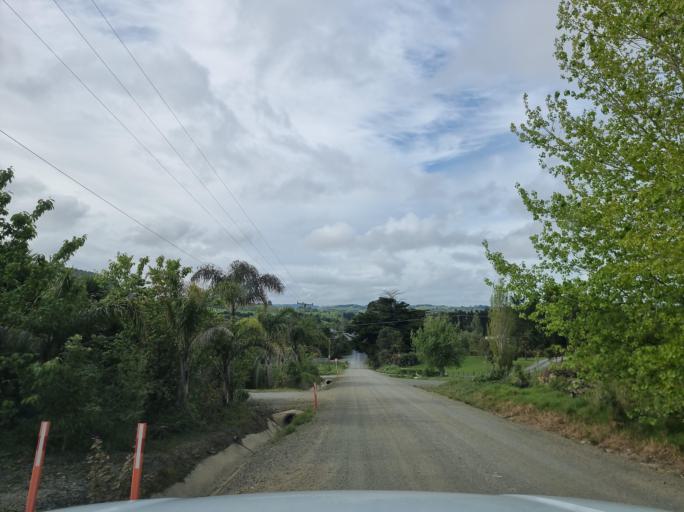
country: NZ
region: Northland
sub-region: Whangarei
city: Ruakaka
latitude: -36.0995
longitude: 174.3667
